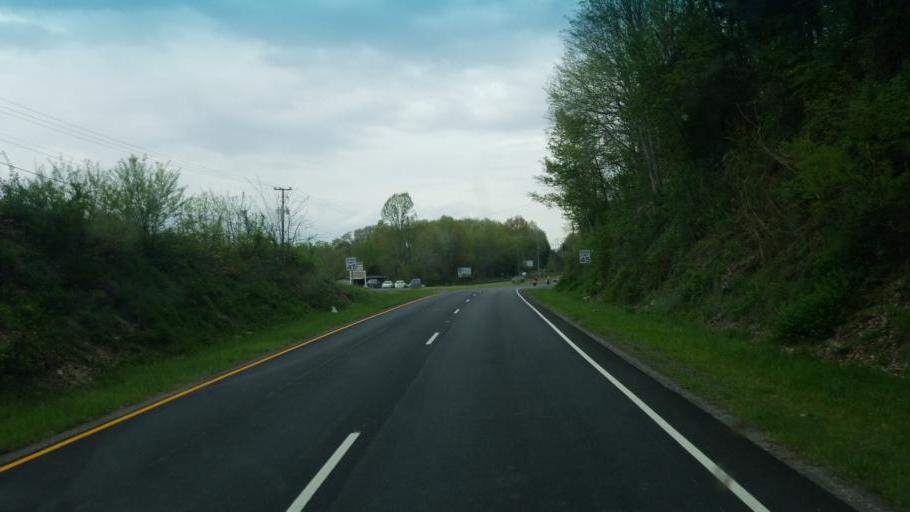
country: US
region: Virginia
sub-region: Smyth County
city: Marion
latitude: 36.8234
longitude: -81.5392
